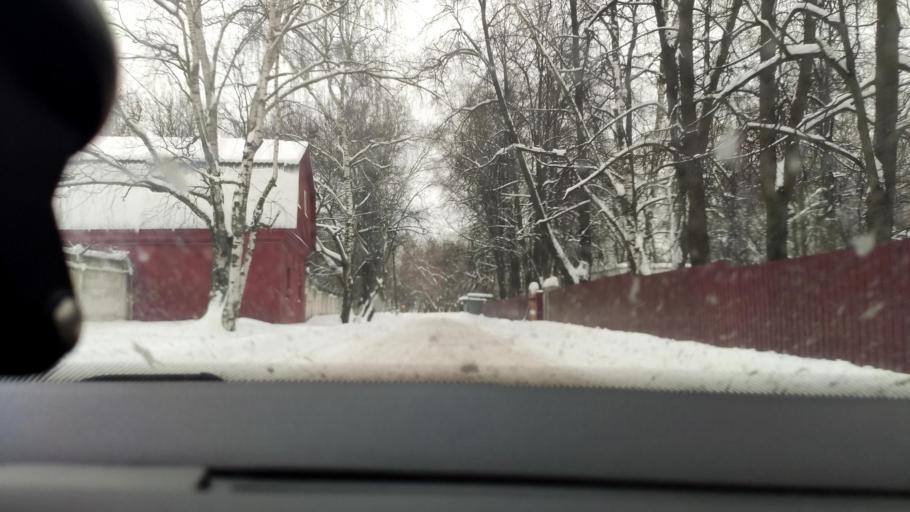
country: RU
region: Moscow
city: Vatutino
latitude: 55.8576
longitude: 37.7000
